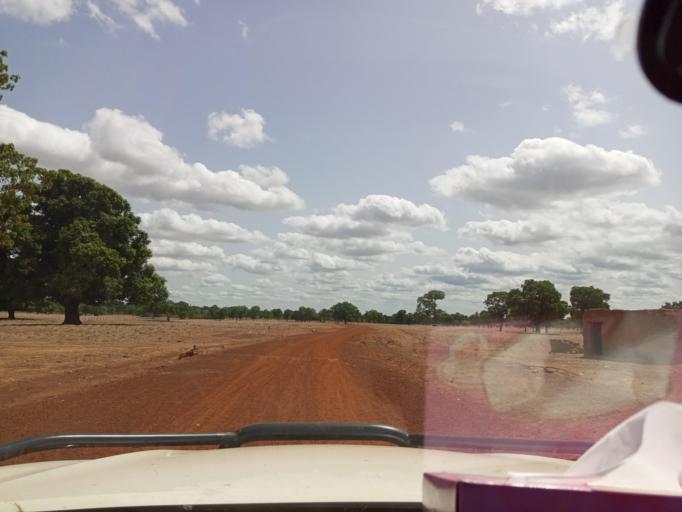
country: ML
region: Sikasso
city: Kolondieba
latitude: 11.5619
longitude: -6.7006
